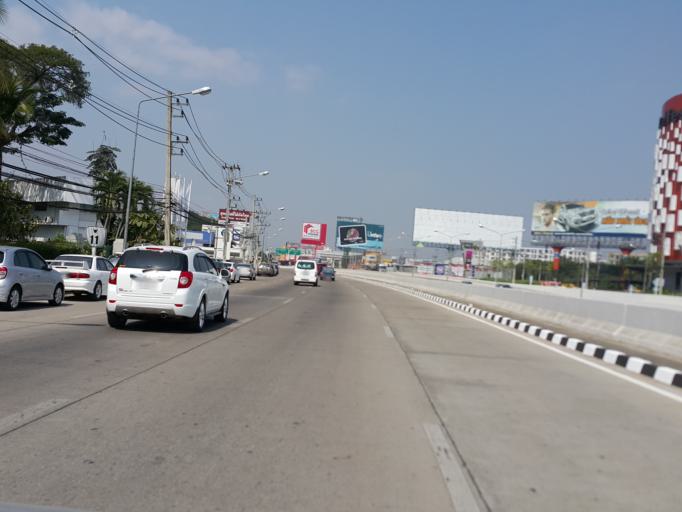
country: TH
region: Chiang Mai
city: Chiang Mai
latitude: 18.8046
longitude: 99.0177
